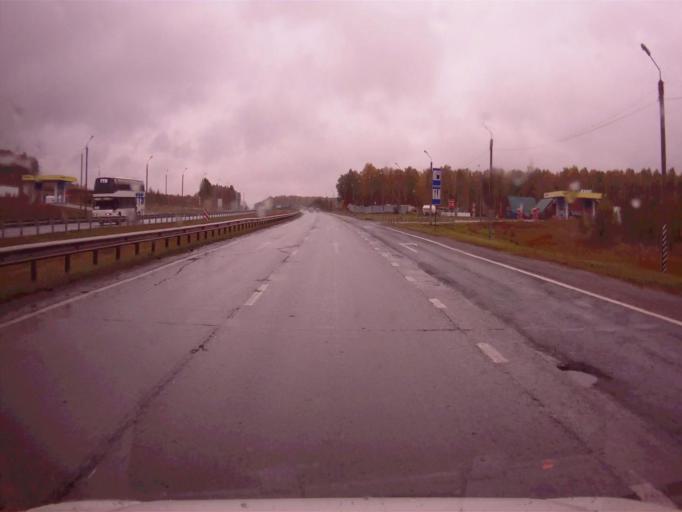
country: RU
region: Chelyabinsk
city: Dolgoderevenskoye
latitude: 55.3253
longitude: 61.3295
